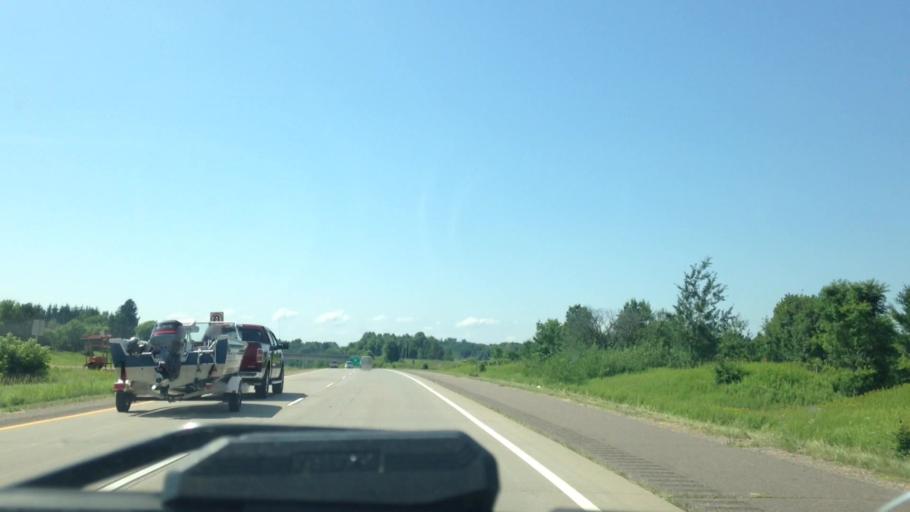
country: US
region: Wisconsin
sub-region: Barron County
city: Rice Lake
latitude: 45.4993
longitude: -91.7644
